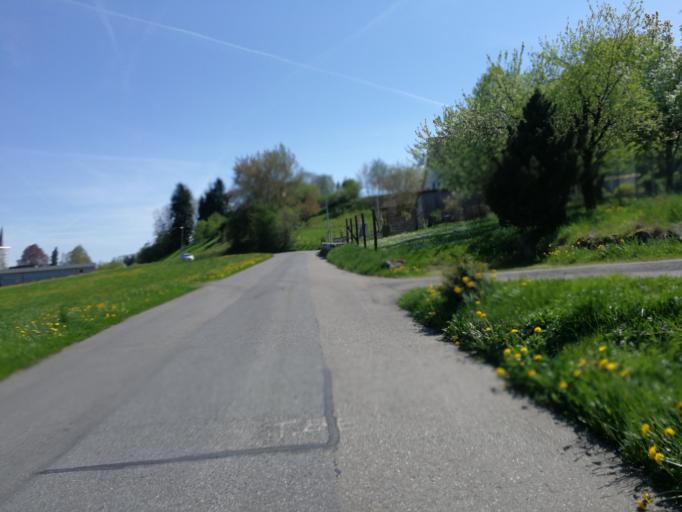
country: CH
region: Zurich
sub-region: Bezirk Hinwil
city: Bubikon
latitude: 47.2705
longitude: 8.8124
